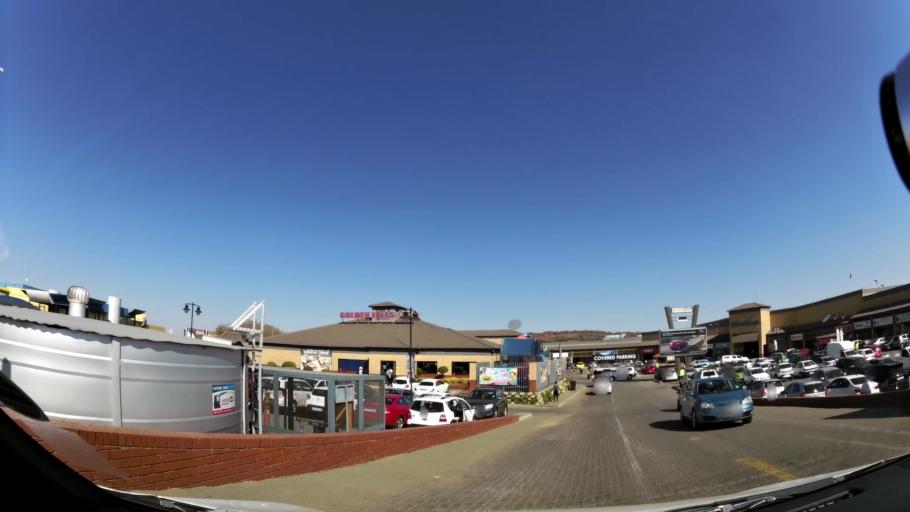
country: ZA
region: Gauteng
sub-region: City of Johannesburg Metropolitan Municipality
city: Johannesburg
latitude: -26.2719
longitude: 28.0296
